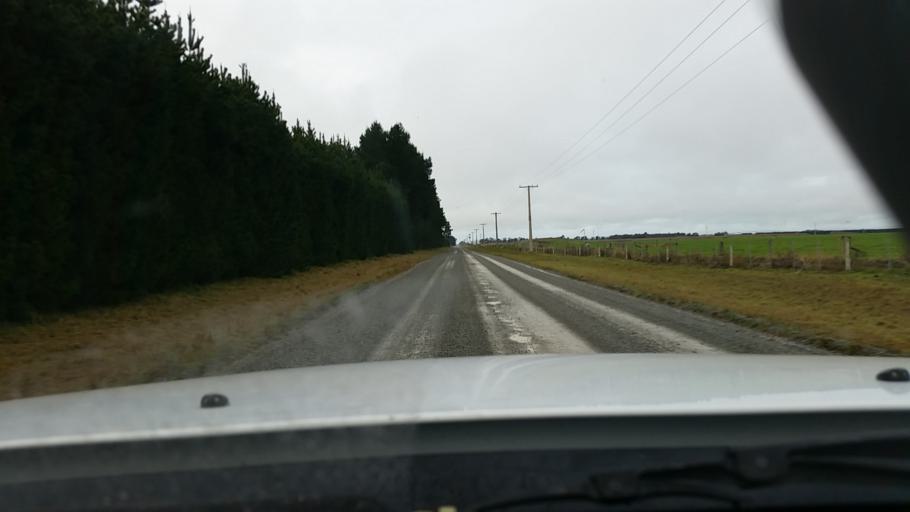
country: NZ
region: Canterbury
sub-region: Timaru District
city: Pleasant Point
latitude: -44.1004
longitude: 171.3740
